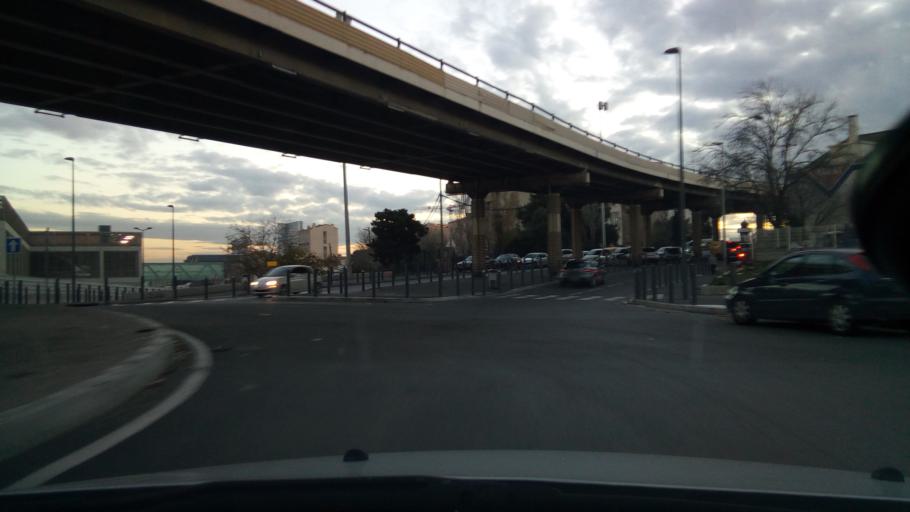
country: FR
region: Provence-Alpes-Cote d'Azur
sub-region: Departement des Bouches-du-Rhone
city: Marseille 14
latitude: 43.3294
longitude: 5.3668
